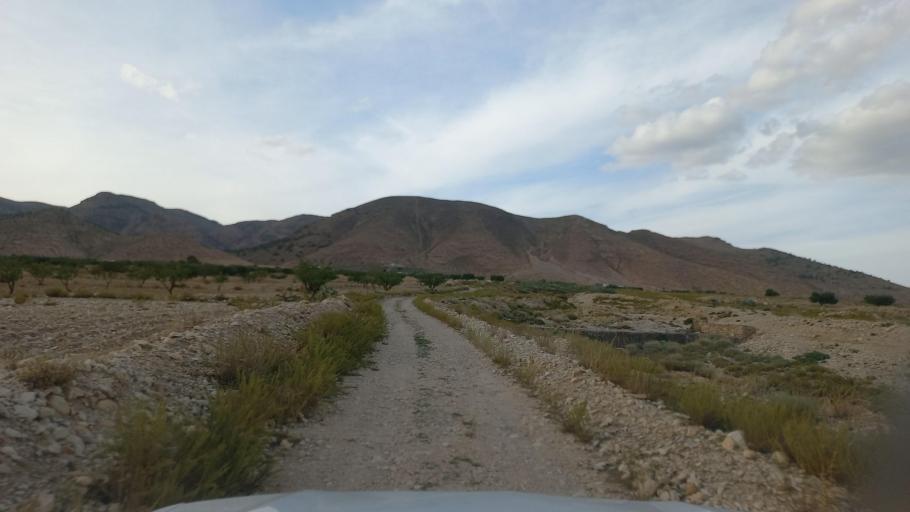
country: TN
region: Al Qasrayn
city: Sbiba
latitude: 35.4468
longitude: 9.0675
